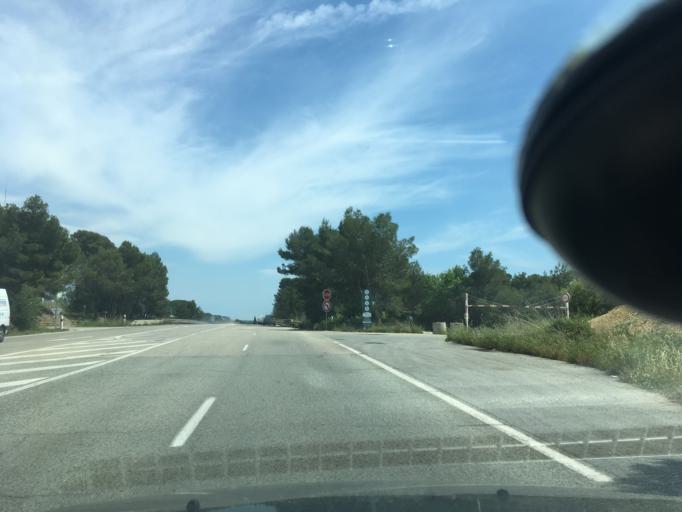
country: FR
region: Provence-Alpes-Cote d'Azur
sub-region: Departement du Var
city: Roquebrune-sur-Argens
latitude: 43.4645
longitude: 6.6217
